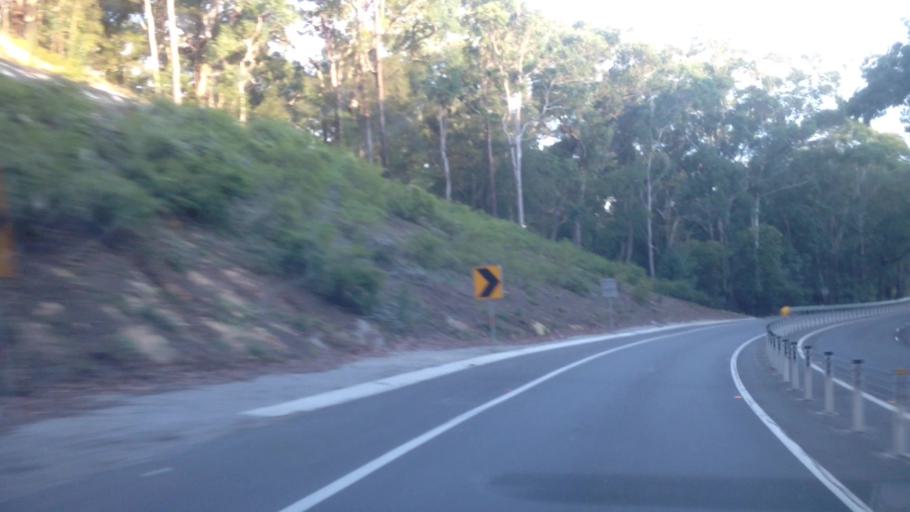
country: AU
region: New South Wales
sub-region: Lake Macquarie Shire
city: Cooranbong
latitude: -32.9706
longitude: 151.4823
